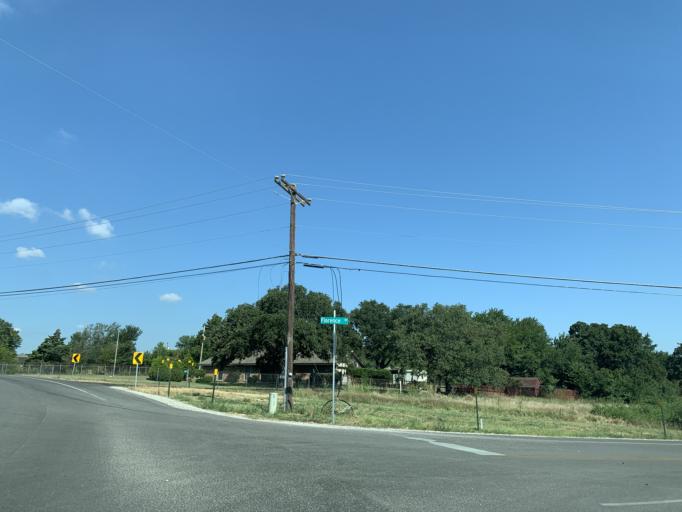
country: US
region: Texas
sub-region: Tarrant County
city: Azle
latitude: 32.8596
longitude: -97.5231
